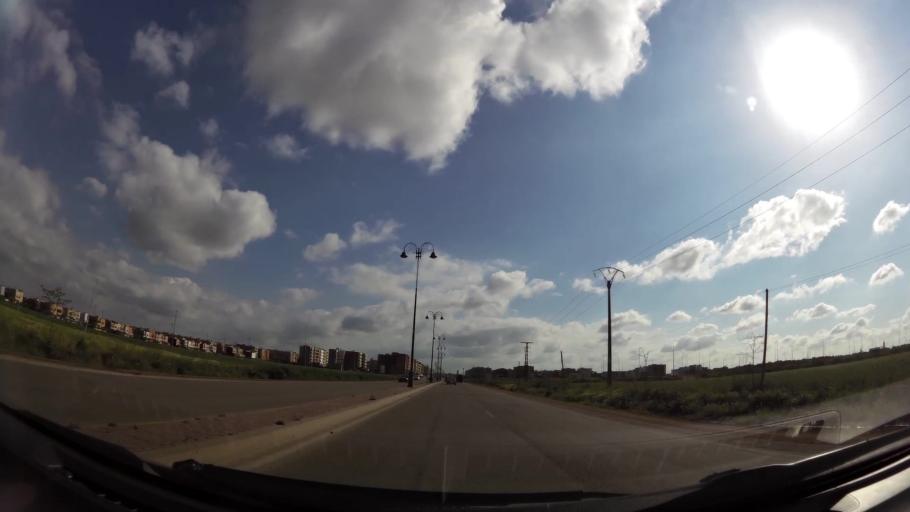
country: MA
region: Chaouia-Ouardigha
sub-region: Settat Province
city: Berrechid
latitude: 33.2823
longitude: -7.5793
